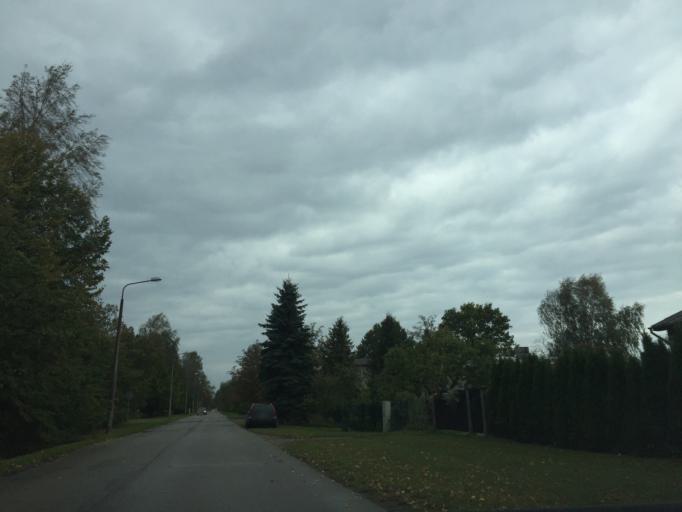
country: LV
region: Jelgava
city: Jelgava
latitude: 56.7477
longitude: 23.6765
